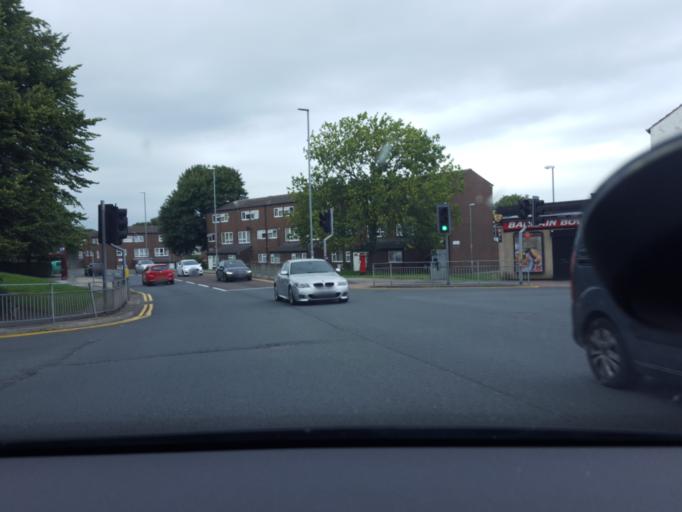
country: GB
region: England
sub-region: City and Borough of Leeds
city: Horsforth
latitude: 53.8078
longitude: -1.6242
